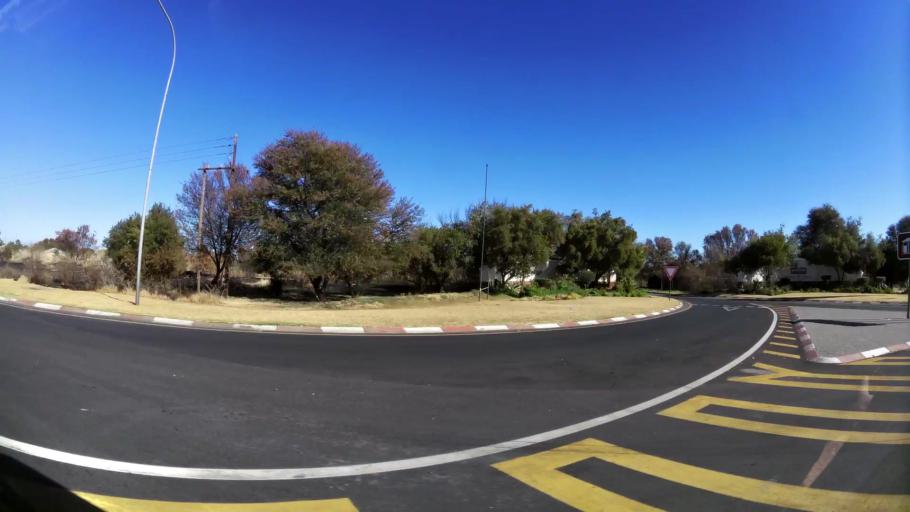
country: ZA
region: Northern Cape
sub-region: Frances Baard District Municipality
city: Kimberley
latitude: -28.6916
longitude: 24.7782
